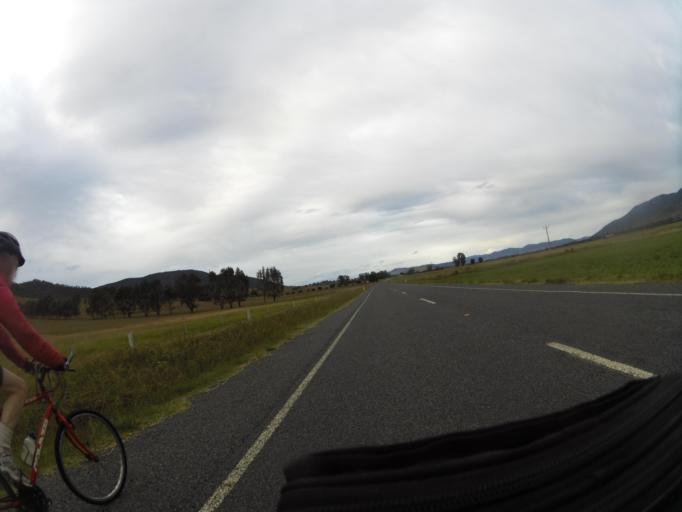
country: AU
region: New South Wales
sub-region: Snowy River
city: Jindabyne
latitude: -36.1372
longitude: 147.9738
